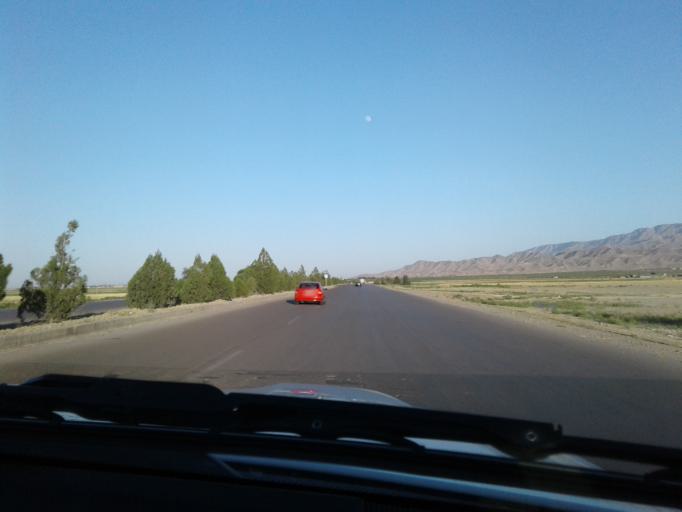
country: TM
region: Ahal
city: Baharly
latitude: 38.2956
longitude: 57.6401
